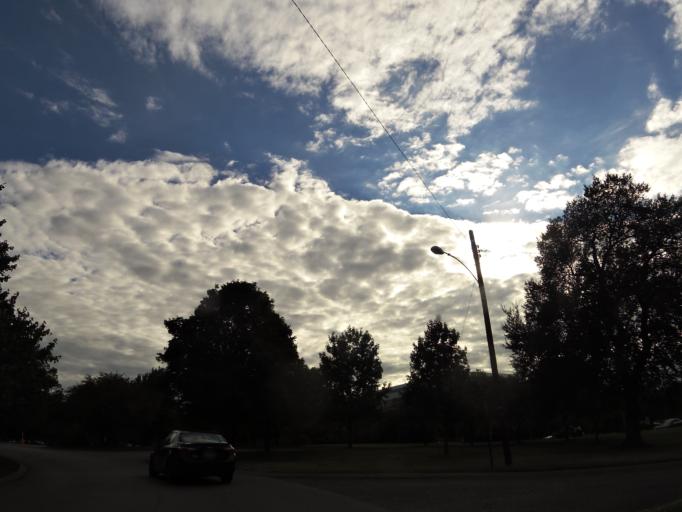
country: US
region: Tennessee
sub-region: Davidson County
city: Nashville
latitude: 36.1528
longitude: -86.8134
